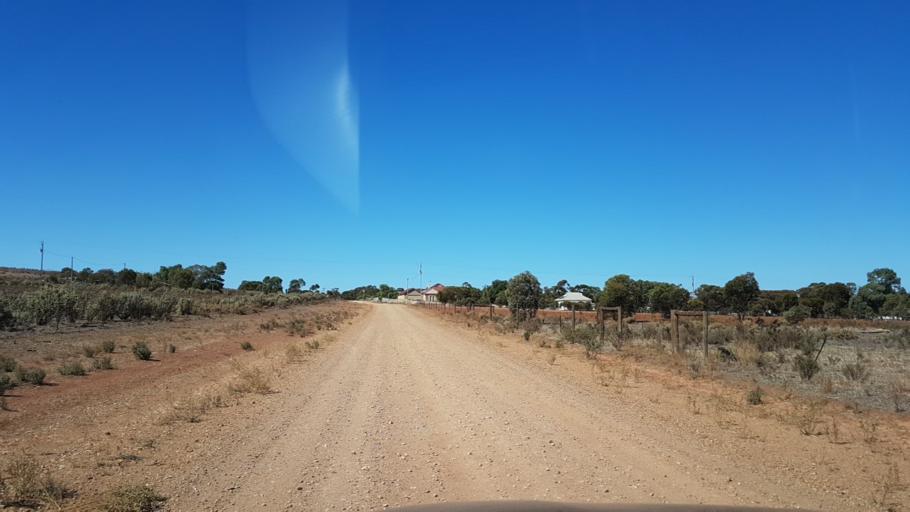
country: AU
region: South Australia
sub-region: Peterborough
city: Peterborough
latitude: -32.9696
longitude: 138.8234
